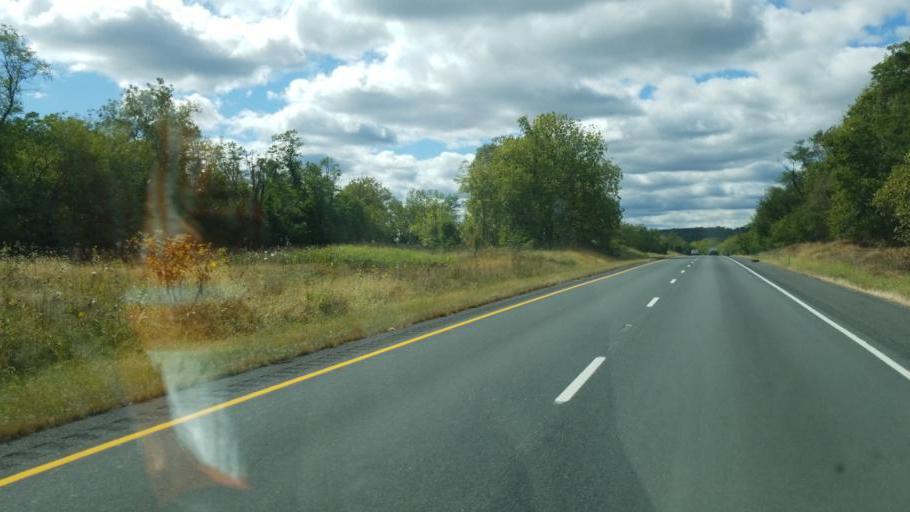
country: US
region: Maryland
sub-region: Washington County
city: Wilson-Conococheague
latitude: 39.6488
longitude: -77.9323
